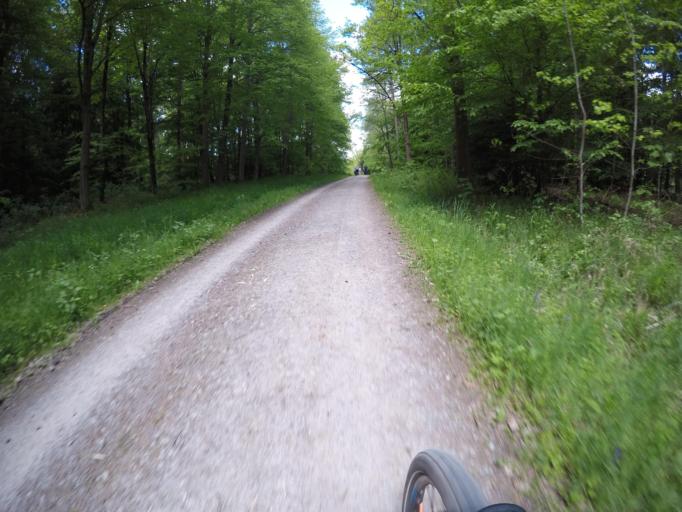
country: DE
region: Baden-Wuerttemberg
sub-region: Regierungsbezirk Stuttgart
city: Gerlingen
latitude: 48.7420
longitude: 9.0637
